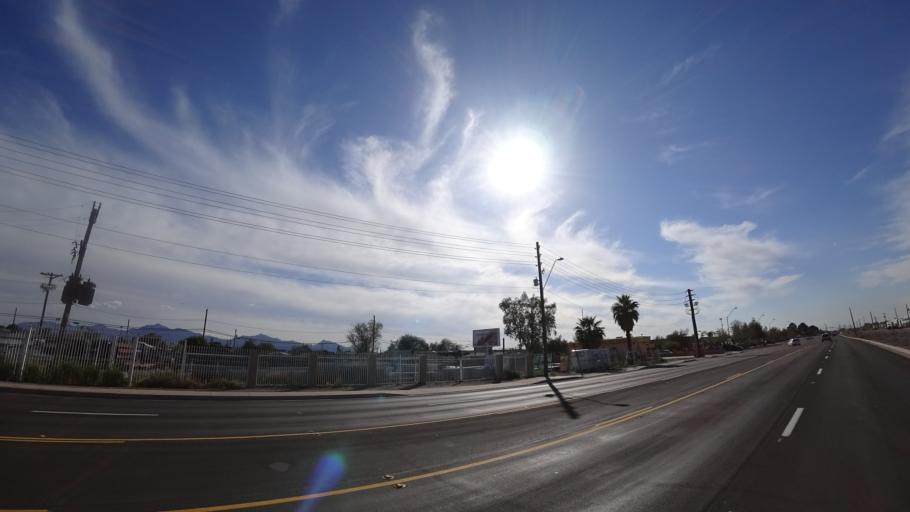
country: US
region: Arizona
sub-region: Maricopa County
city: Tolleson
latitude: 33.4355
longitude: -112.3012
